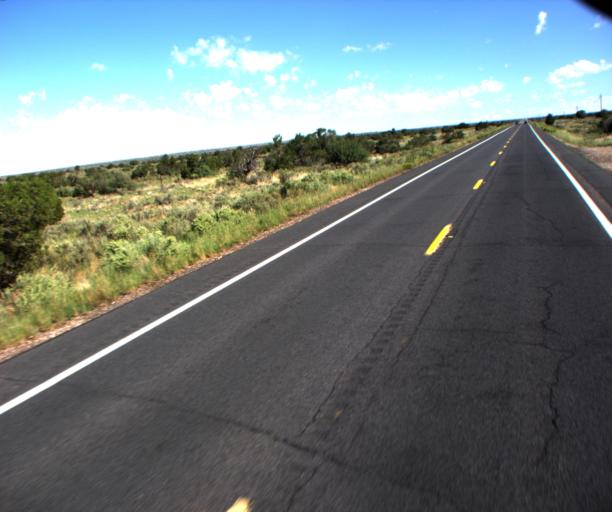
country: US
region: Arizona
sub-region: Coconino County
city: Grand Canyon Village
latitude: 35.7195
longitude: -112.1312
